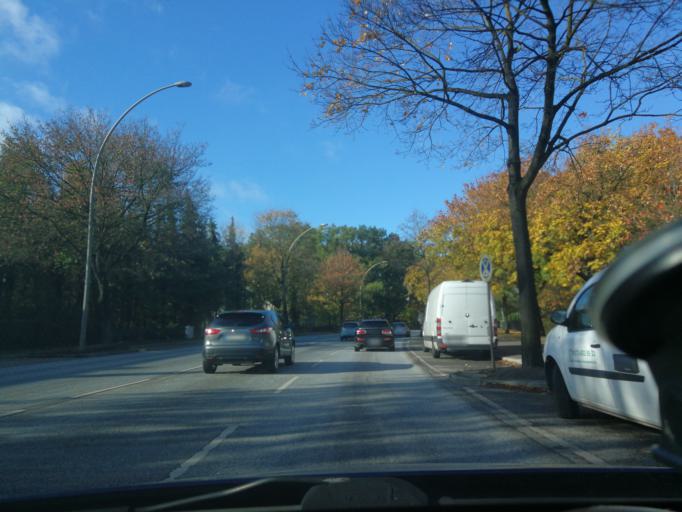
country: DE
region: Lower Saxony
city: Neu Wulmstorf
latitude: 53.4715
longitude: 9.8595
